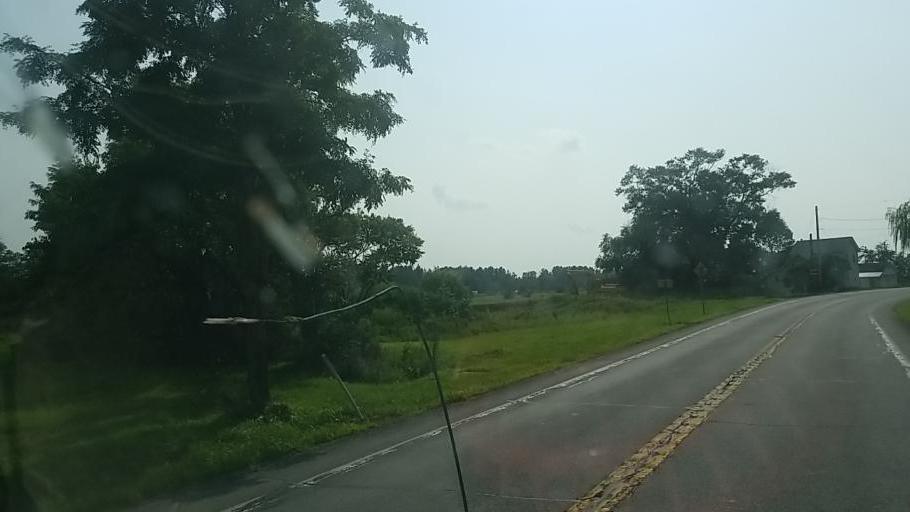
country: US
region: New York
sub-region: Montgomery County
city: Tribes Hill
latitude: 42.9352
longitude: -74.2490
